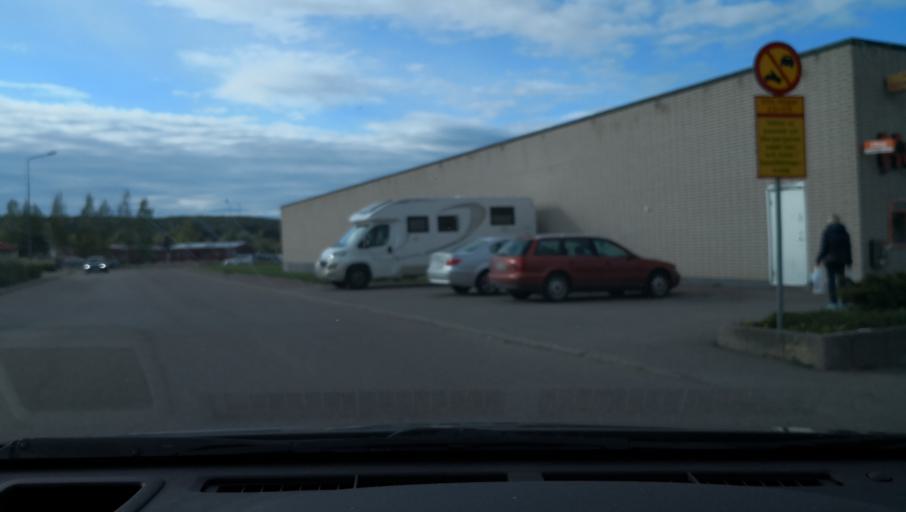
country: SE
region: Dalarna
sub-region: Hedemora Kommun
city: Hedemora
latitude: 60.2828
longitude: 15.9896
